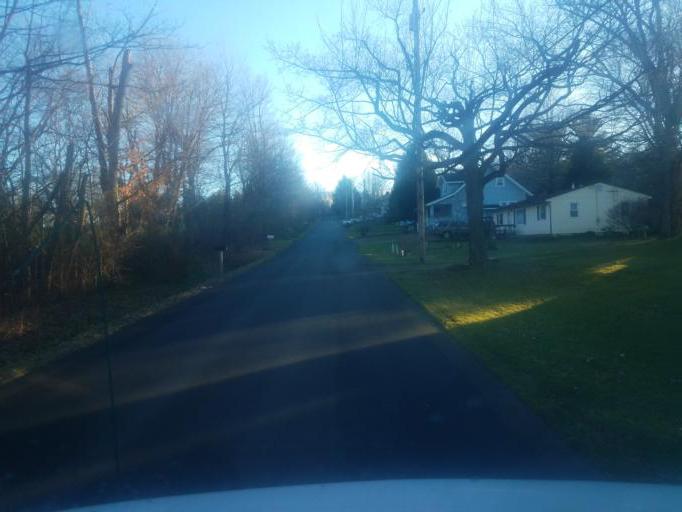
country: US
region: Ohio
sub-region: Richland County
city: Mansfield
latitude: 40.7853
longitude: -82.5425
